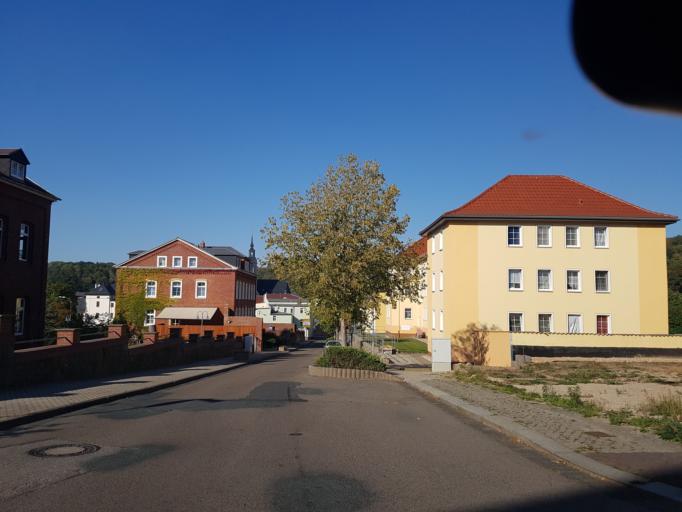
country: DE
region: Saxony
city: Waldheim
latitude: 51.0718
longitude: 13.0287
